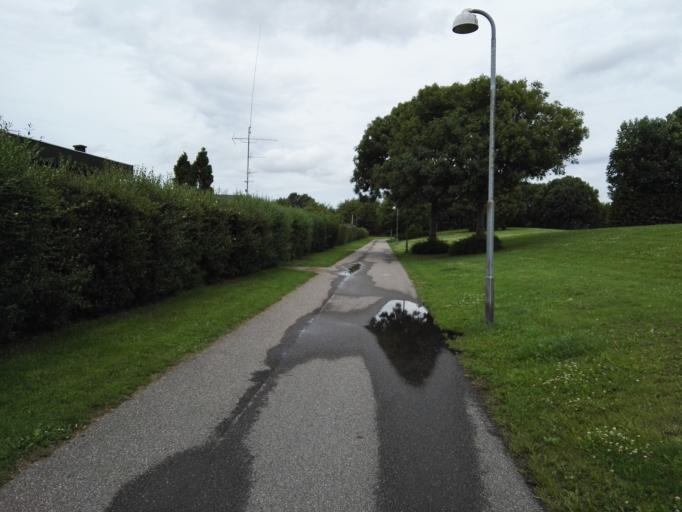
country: DK
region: Capital Region
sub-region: Egedal Kommune
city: Olstykke
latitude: 55.7781
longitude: 12.1682
